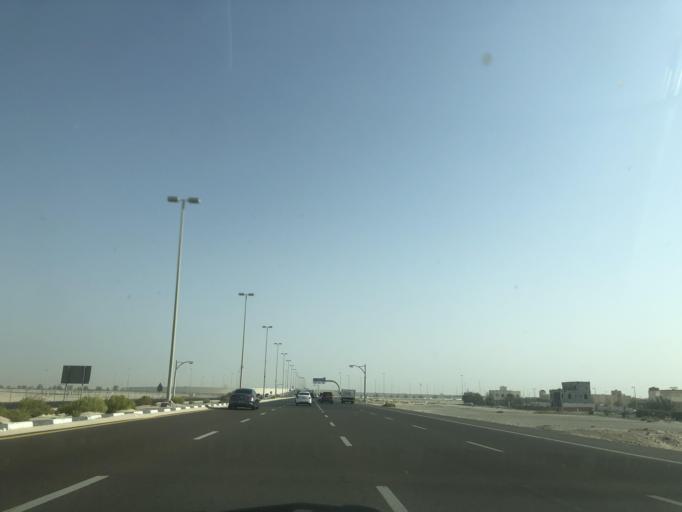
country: AE
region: Abu Dhabi
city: Abu Dhabi
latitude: 24.4060
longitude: 54.7158
